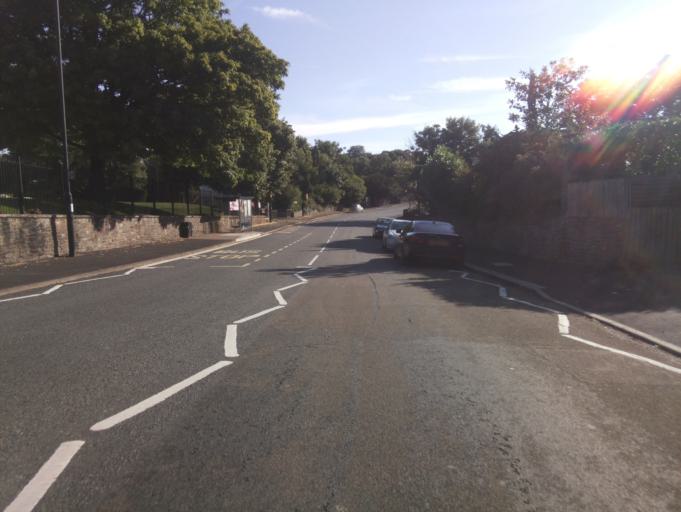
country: GB
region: England
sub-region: Bath and North East Somerset
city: Whitchurch
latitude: 51.4280
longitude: -2.5552
